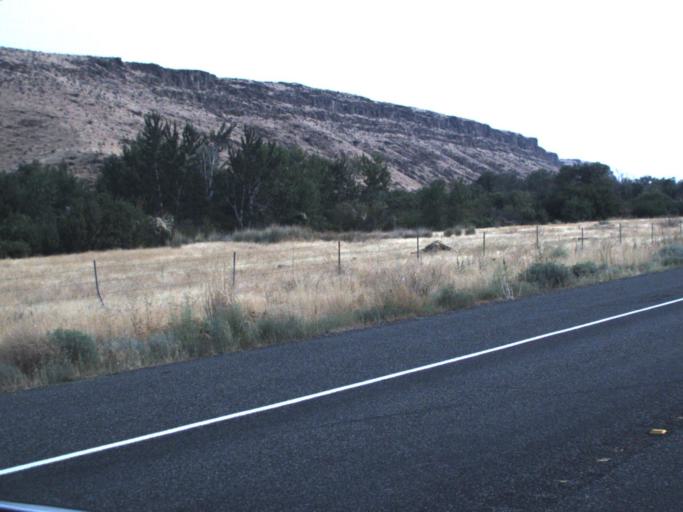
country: US
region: Washington
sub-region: Yakima County
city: Toppenish
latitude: 46.2165
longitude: -120.4447
